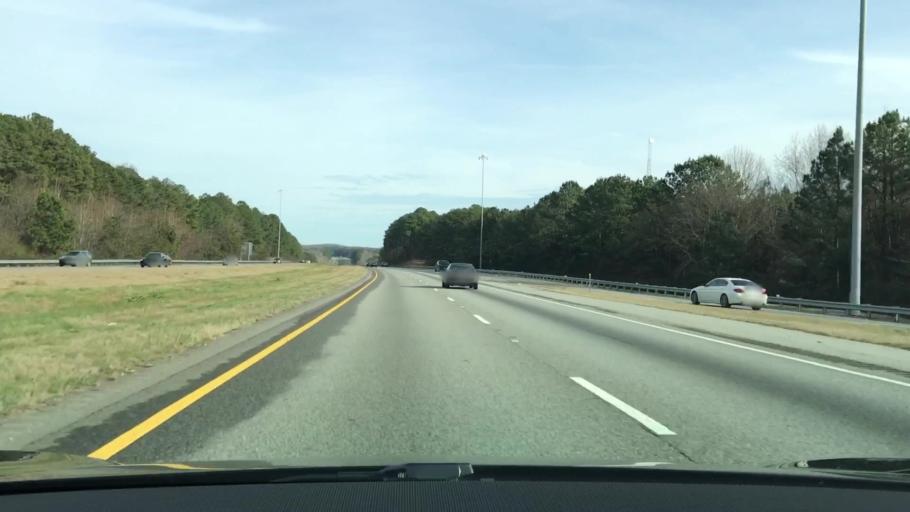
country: US
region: Georgia
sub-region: Newton County
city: Covington
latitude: 33.6120
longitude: -83.8216
